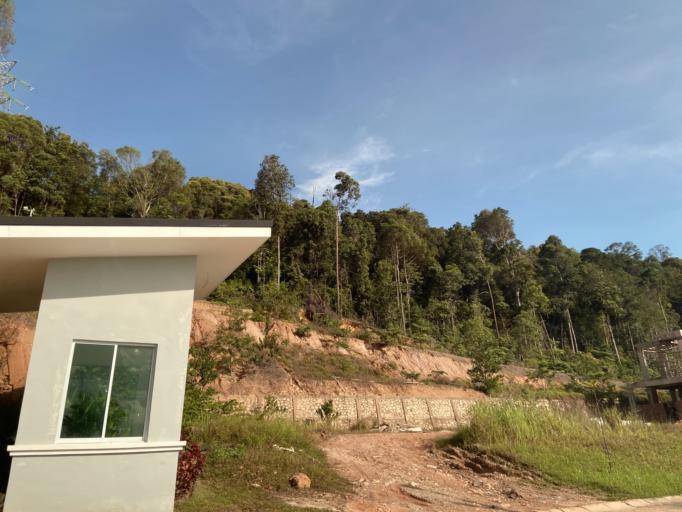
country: SG
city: Singapore
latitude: 1.0921
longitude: 104.0265
